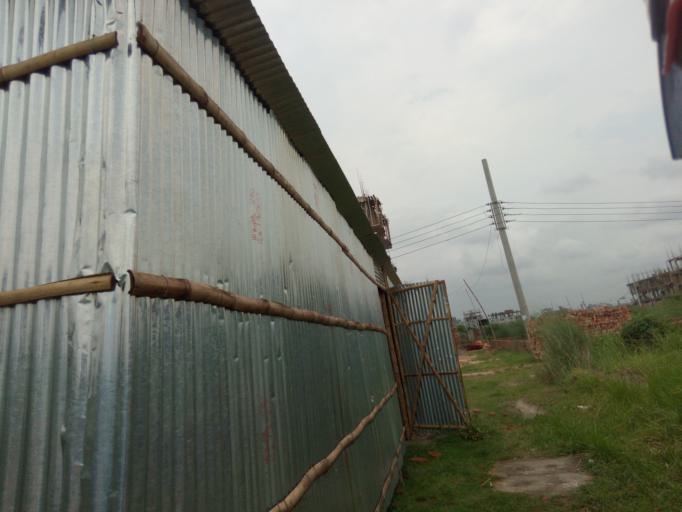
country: BD
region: Dhaka
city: Azimpur
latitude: 23.7505
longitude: 90.3484
